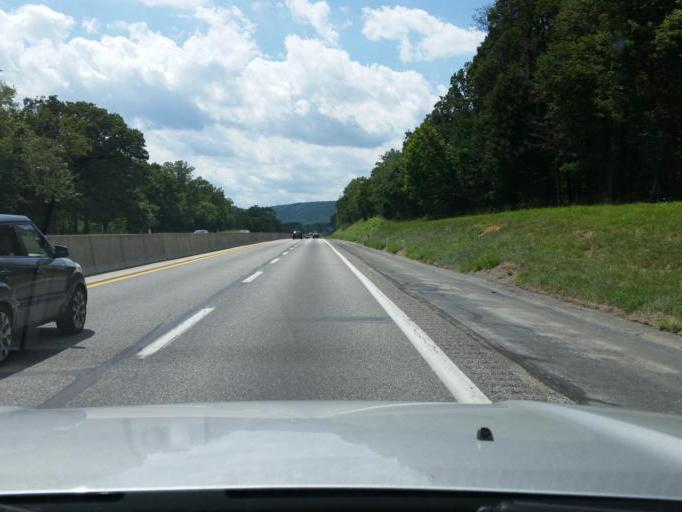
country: US
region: Pennsylvania
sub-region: Cumberland County
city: Shippensburg
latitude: 40.1682
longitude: -77.5803
